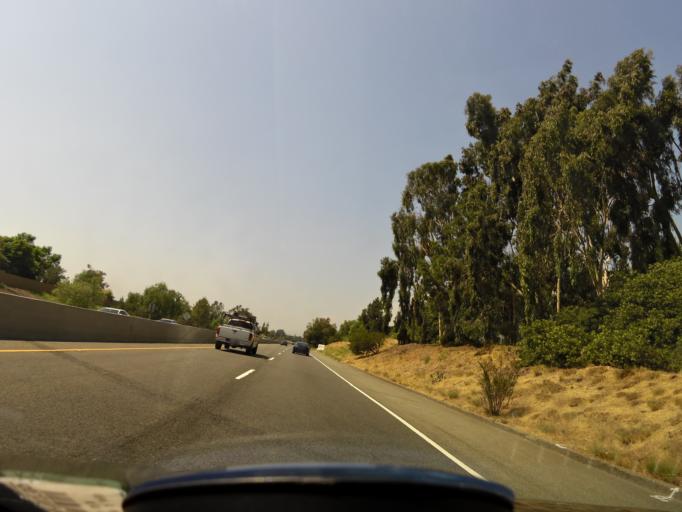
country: US
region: California
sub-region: Orange County
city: Yorba Linda
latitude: 33.8687
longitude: -117.7947
